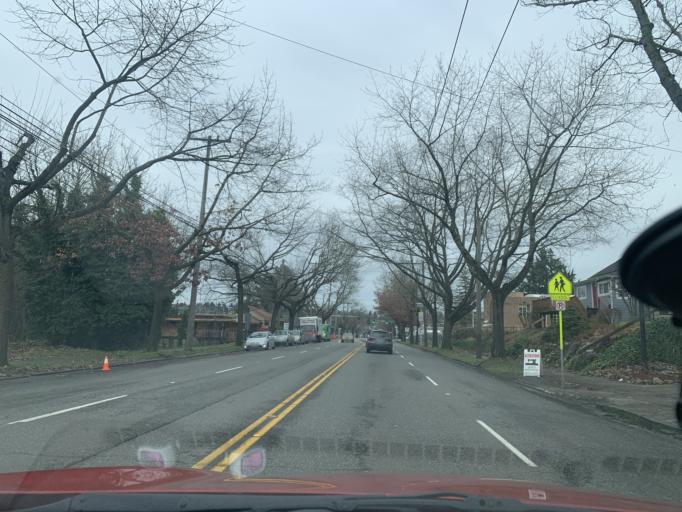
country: US
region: Washington
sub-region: King County
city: Bryn Mawr-Skyway
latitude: 47.5277
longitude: -122.2701
